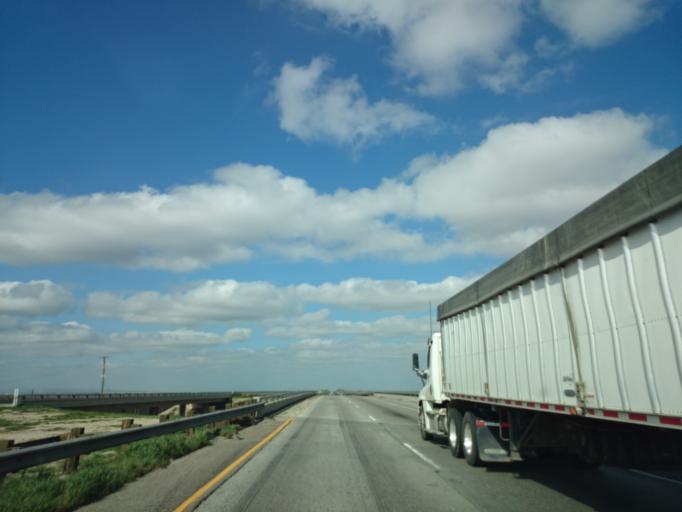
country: US
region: California
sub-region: Kern County
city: Greenfield
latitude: 35.1794
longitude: -119.1302
